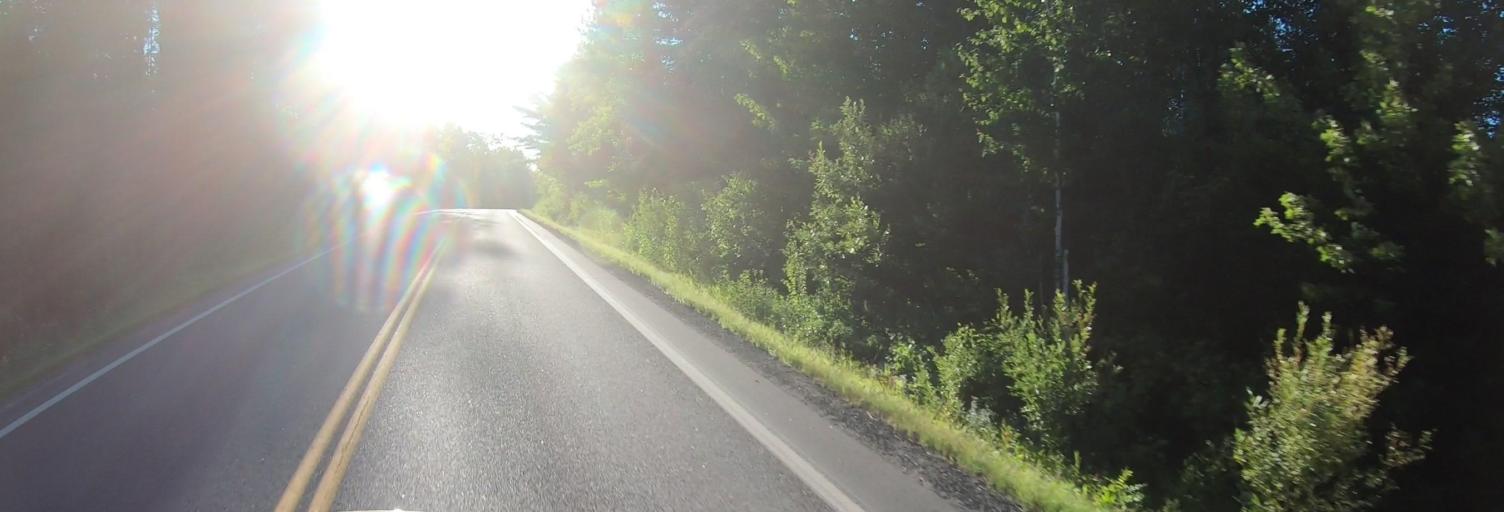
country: US
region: Minnesota
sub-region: Saint Louis County
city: Ely
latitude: 47.9574
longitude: -91.6163
